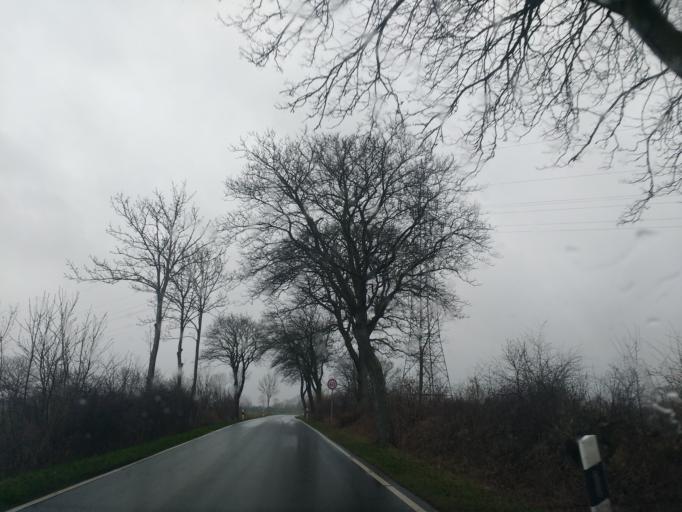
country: DE
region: Schleswig-Holstein
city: Gremersdorf
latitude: 54.3106
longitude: 10.9363
